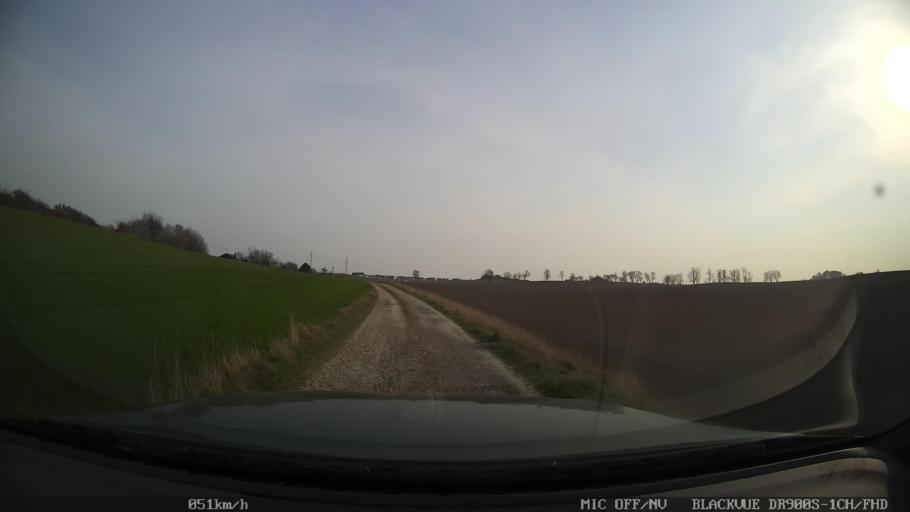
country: SE
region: Skane
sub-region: Ystads Kommun
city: Ystad
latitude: 55.4539
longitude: 13.7932
